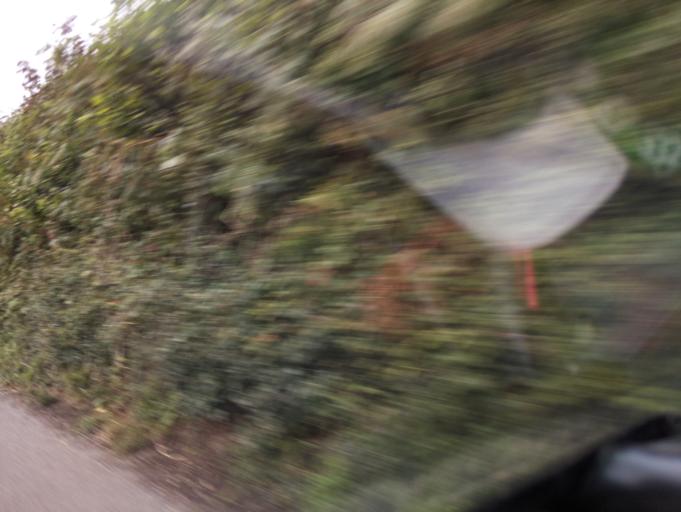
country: GB
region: England
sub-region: Devon
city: Kingsbridge
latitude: 50.2917
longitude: -3.7839
